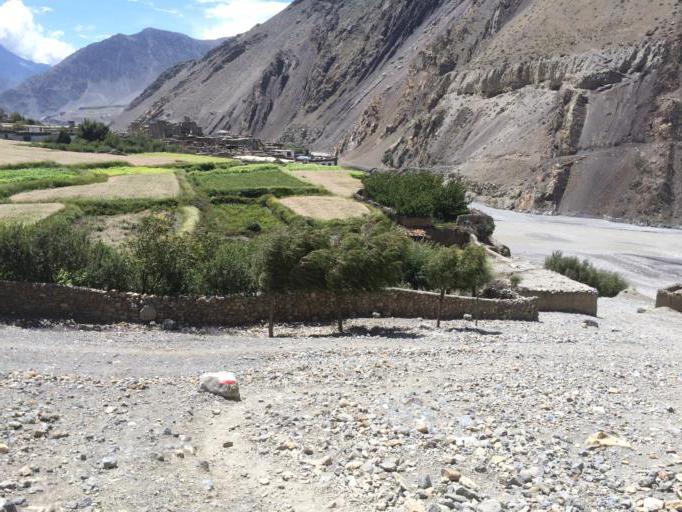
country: NP
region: Western Region
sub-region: Dhawalagiri Zone
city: Jomsom
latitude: 28.8401
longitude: 83.7865
